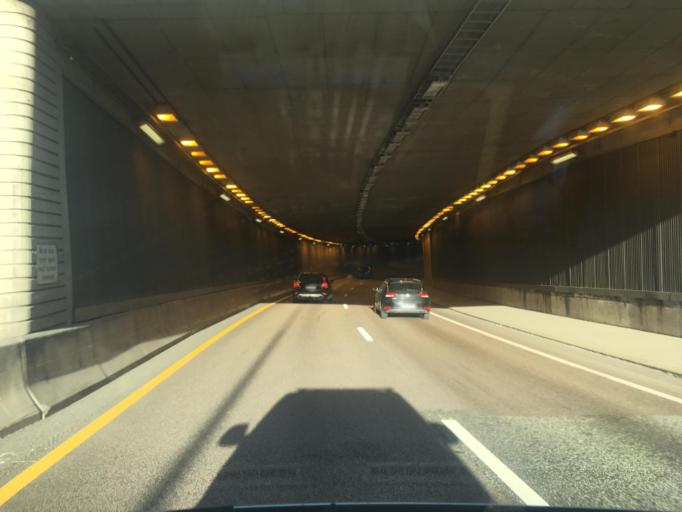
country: NO
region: Oslo
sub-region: Oslo
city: Oslo
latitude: 59.8944
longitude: 10.8045
